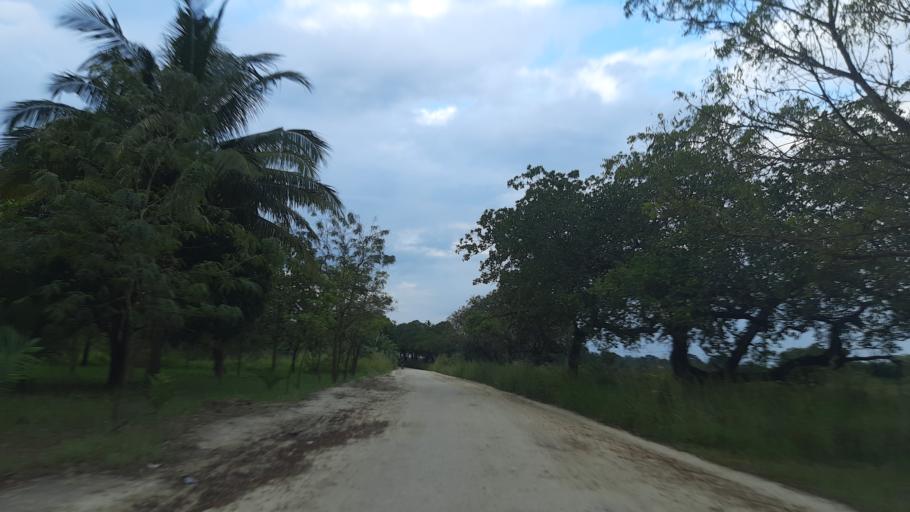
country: TZ
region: Pwani
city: Bagamoyo
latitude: -6.5187
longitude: 38.9276
